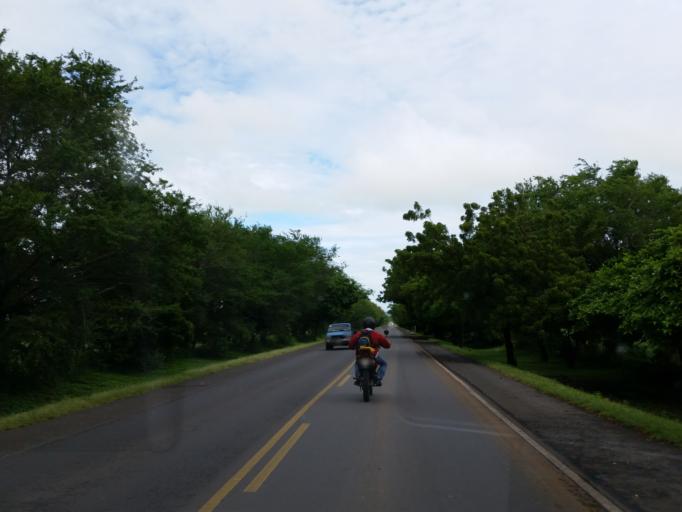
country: NI
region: Leon
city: Nagarote
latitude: 12.2811
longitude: -86.5799
